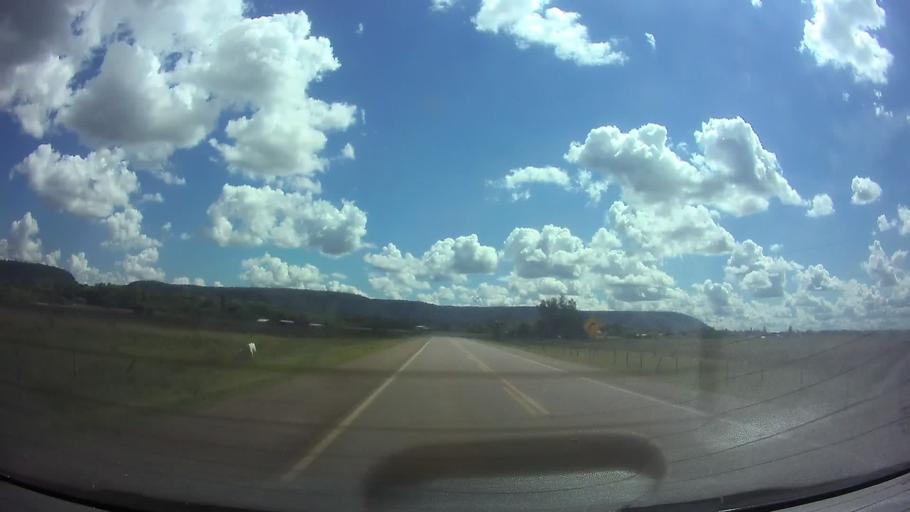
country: PY
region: Guaira
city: Itape
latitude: -25.9158
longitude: -56.6838
